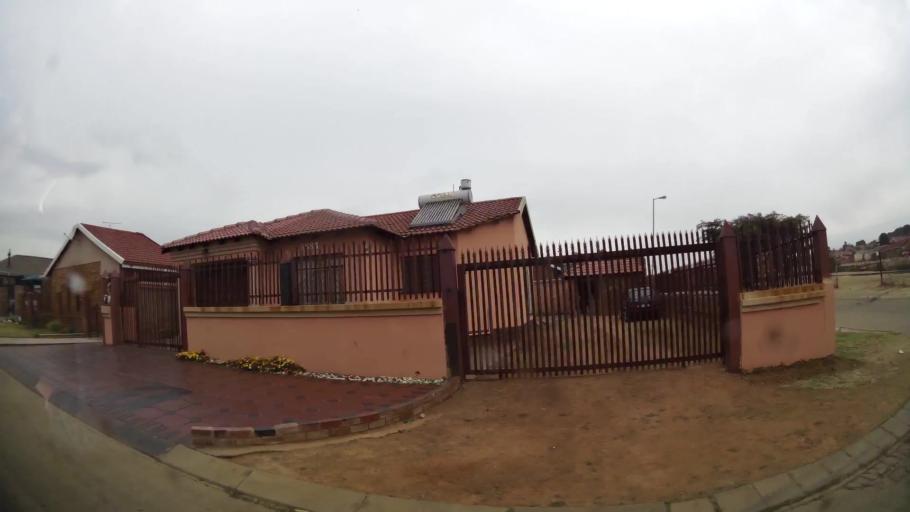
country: ZA
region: Gauteng
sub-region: City of Tshwane Metropolitan Municipality
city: Pretoria
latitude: -25.7059
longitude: 28.3548
